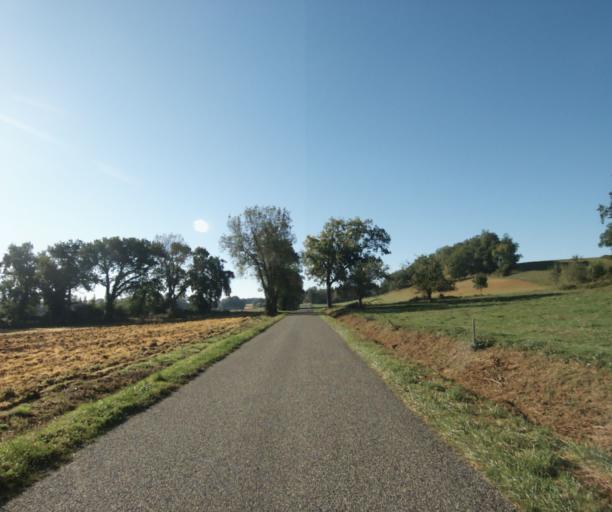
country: FR
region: Midi-Pyrenees
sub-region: Departement du Gers
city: Vic-Fezensac
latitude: 43.8231
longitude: 0.2883
